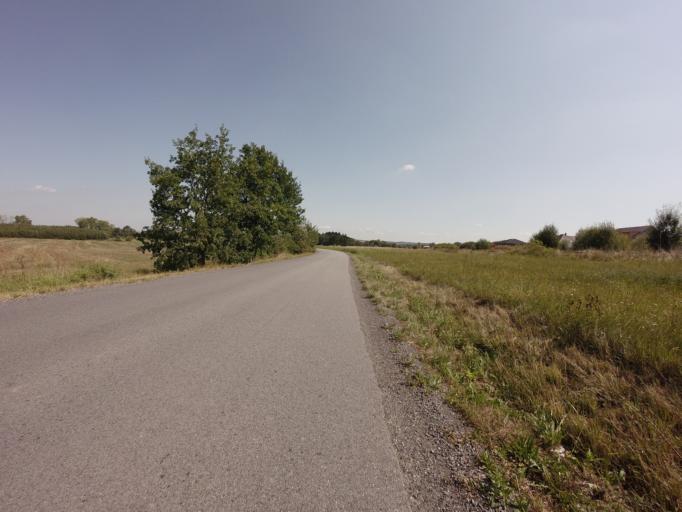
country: CZ
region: Jihocesky
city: Vcelna
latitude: 48.9312
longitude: 14.4540
